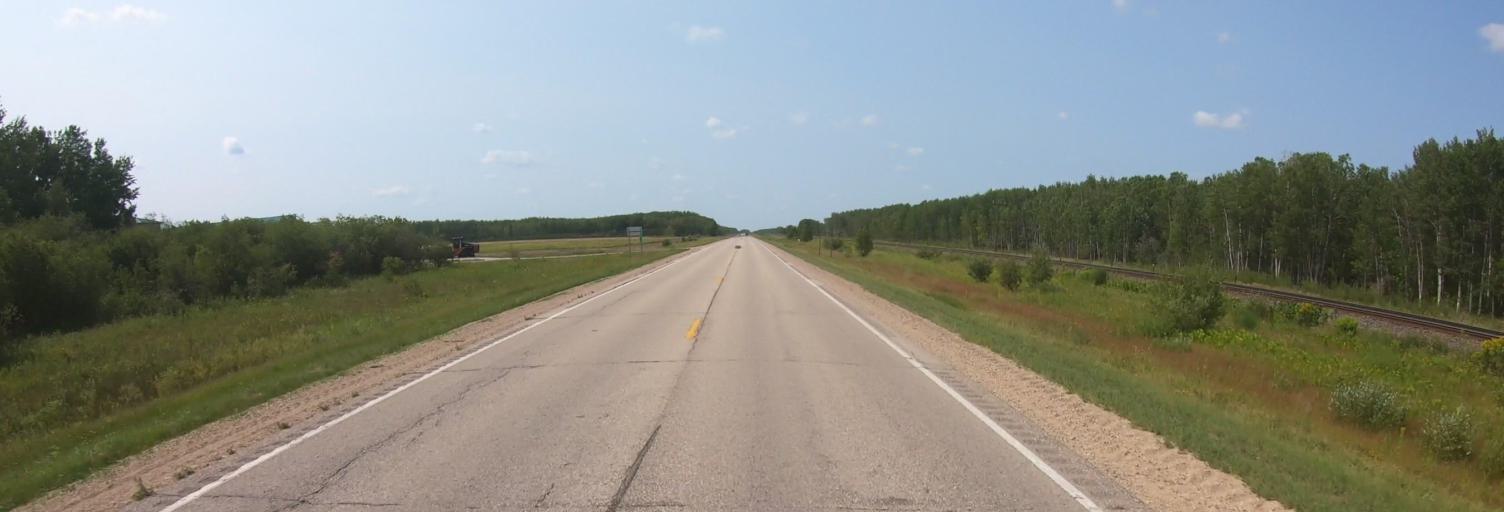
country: US
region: Minnesota
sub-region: Lake of the Woods County
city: Baudette
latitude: 48.7299
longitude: -94.7929
